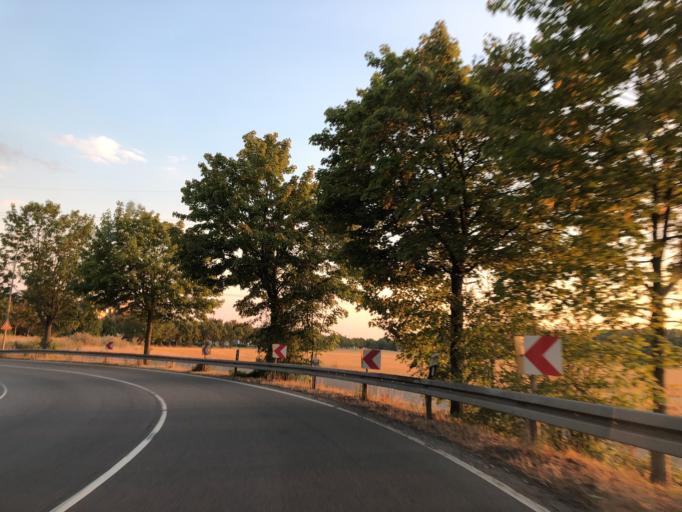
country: DE
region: Hesse
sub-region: Regierungsbezirk Darmstadt
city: Florsheim
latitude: 50.0099
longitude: 8.4139
